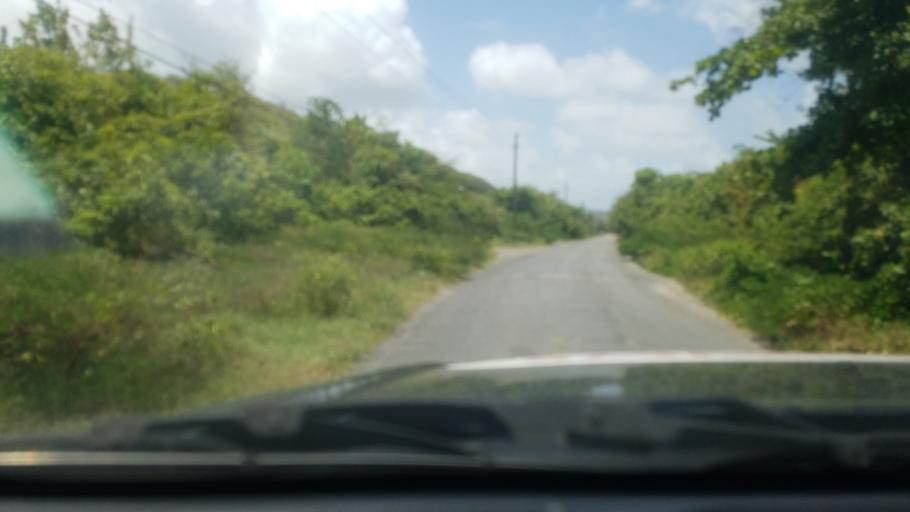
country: LC
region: Vieux-Fort
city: Vieux Fort
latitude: 13.7361
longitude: -60.9435
